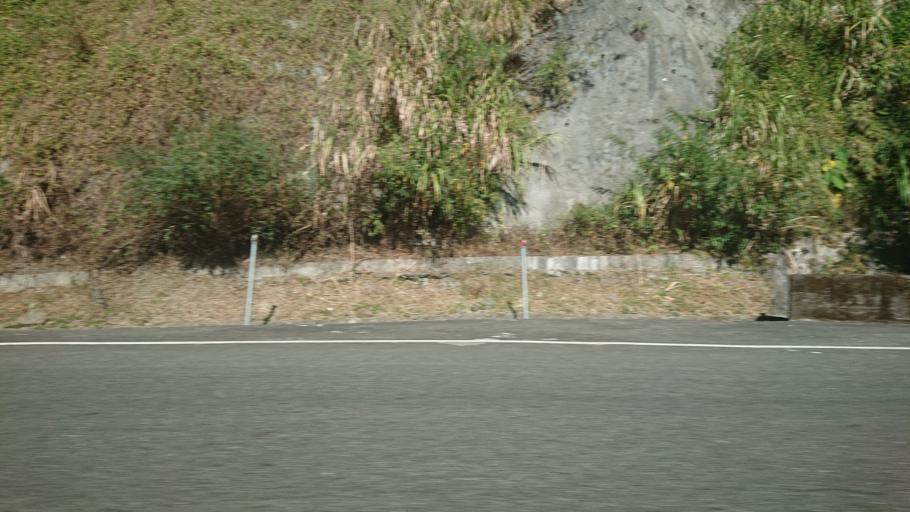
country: TW
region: Taiwan
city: Lugu
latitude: 23.4784
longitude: 120.7351
